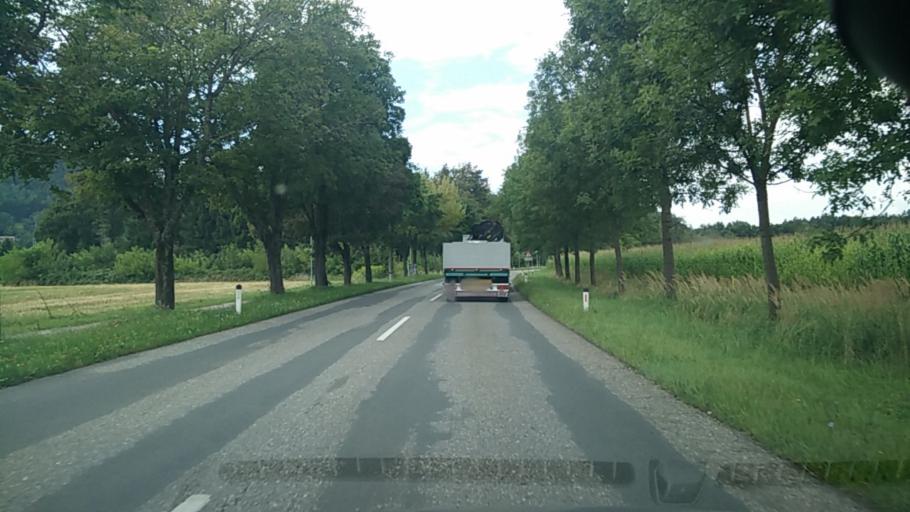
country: AT
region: Carinthia
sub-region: Klagenfurt am Woerthersee
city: Klagenfurt am Woerthersee
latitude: 46.6080
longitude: 14.2691
